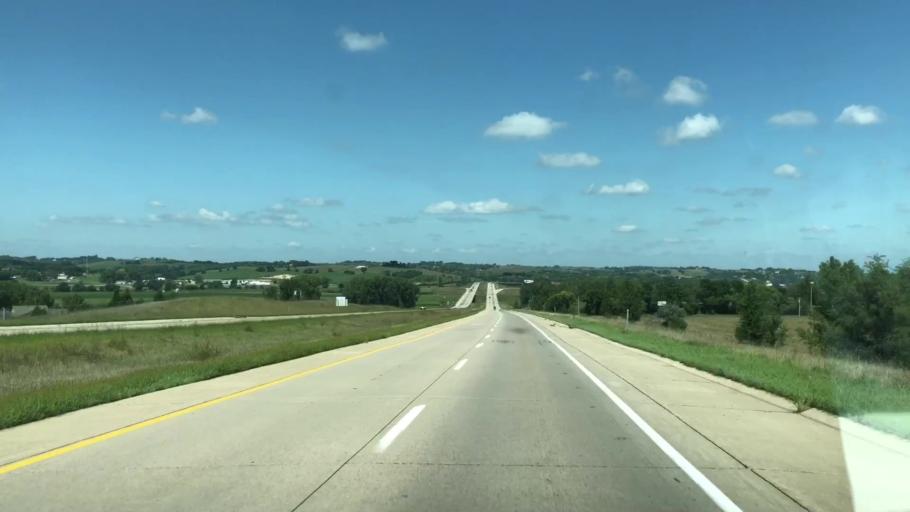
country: US
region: Iowa
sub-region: Woodbury County
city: Sioux City
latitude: 42.5363
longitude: -96.3390
